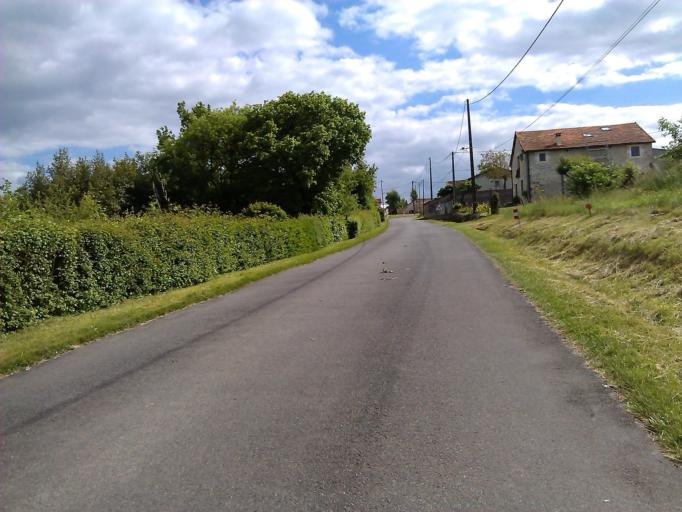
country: FR
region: Poitou-Charentes
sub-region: Departement de la Charente
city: Mansle
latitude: 45.9057
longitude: 0.2178
